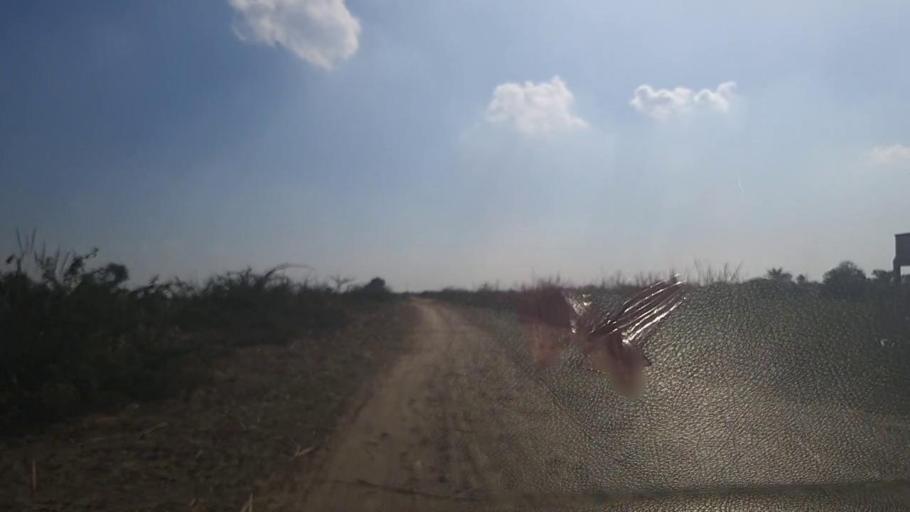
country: PK
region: Sindh
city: Tando Mittha Khan
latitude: 25.7973
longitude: 69.0731
